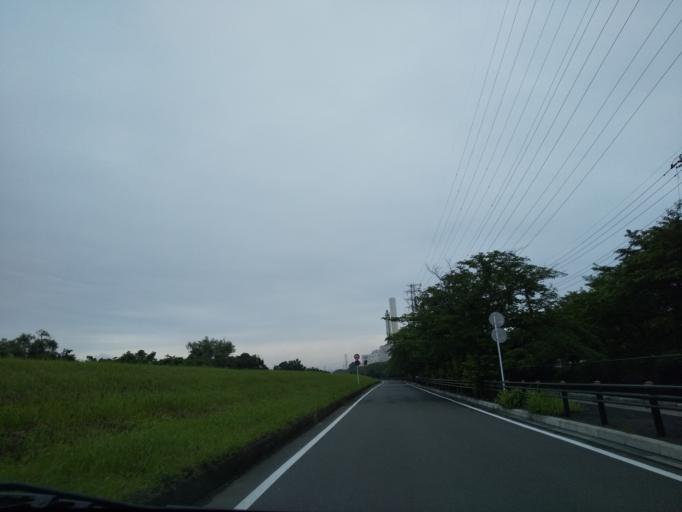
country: JP
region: Tokyo
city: Hino
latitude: 35.6702
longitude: 139.4266
